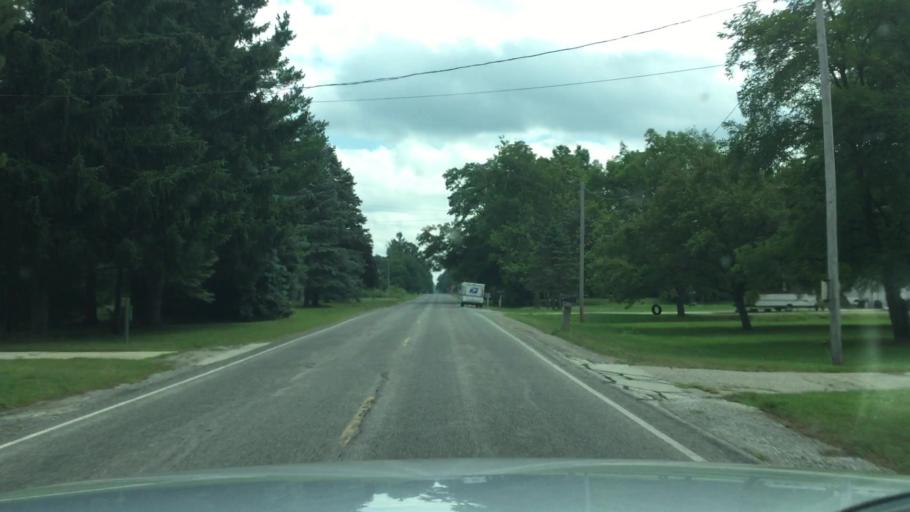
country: US
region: Michigan
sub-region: Saginaw County
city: Birch Run
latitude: 43.2934
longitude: -83.8076
